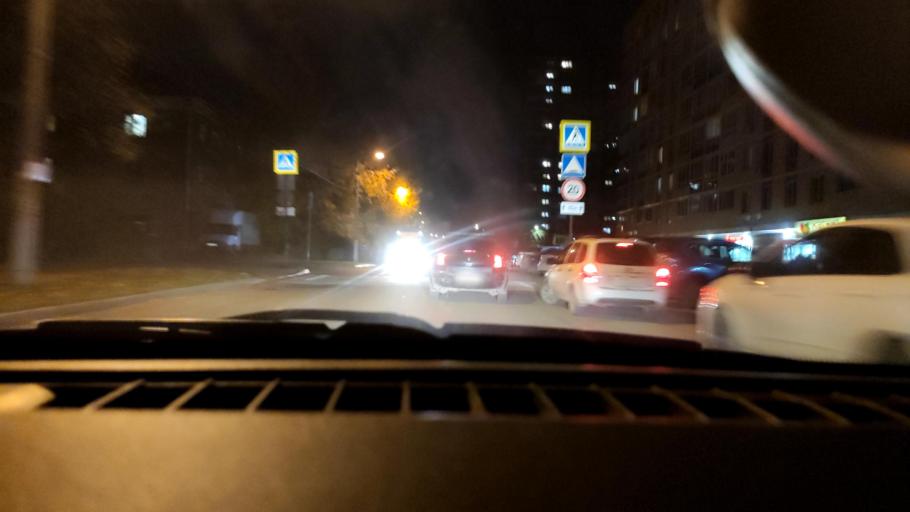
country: RU
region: Perm
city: Kondratovo
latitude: 57.9949
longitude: 56.1480
